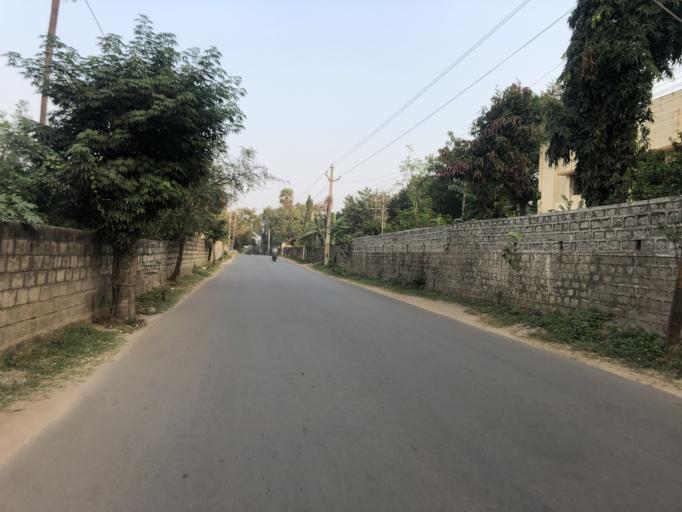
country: IN
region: Telangana
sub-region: Rangareddi
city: Kukatpalli
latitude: 17.4626
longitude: 78.4370
